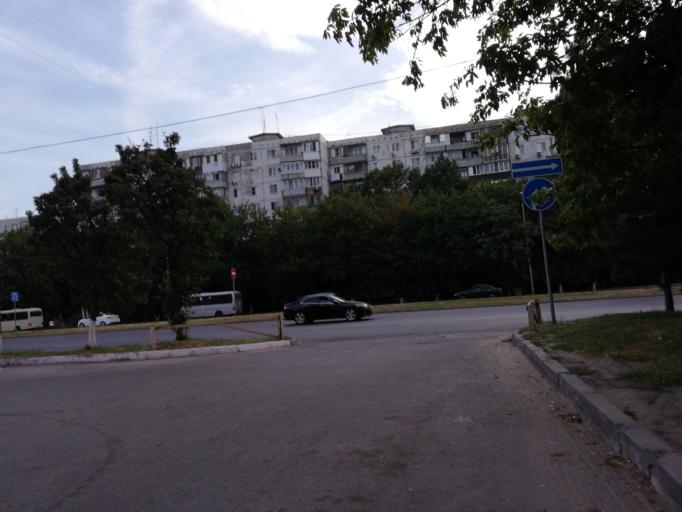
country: RU
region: Rostov
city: Severnyy
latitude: 47.2980
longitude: 39.7131
